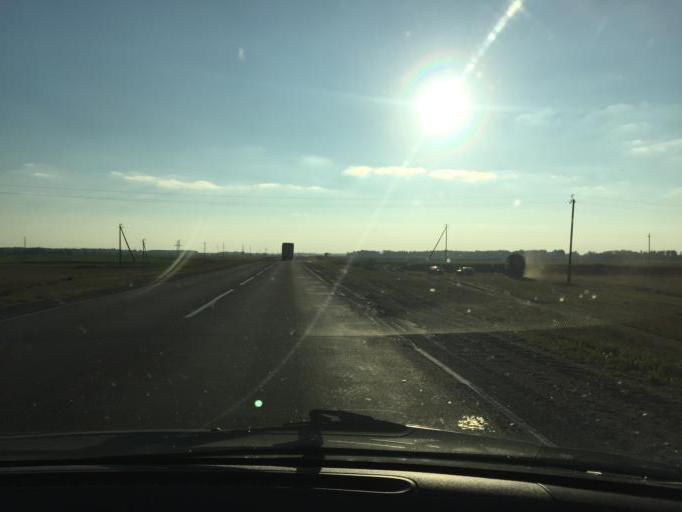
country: BY
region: Brest
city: Asnyezhytsy
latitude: 52.2814
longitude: 26.4037
